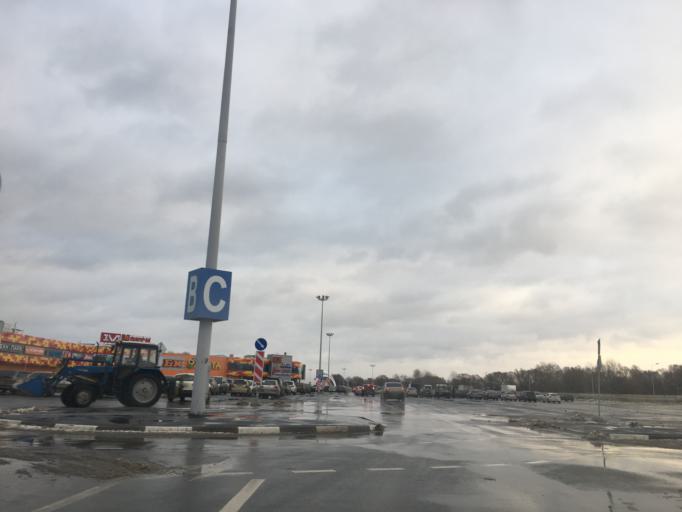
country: RU
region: Tula
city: Tula
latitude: 54.1925
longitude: 37.6347
